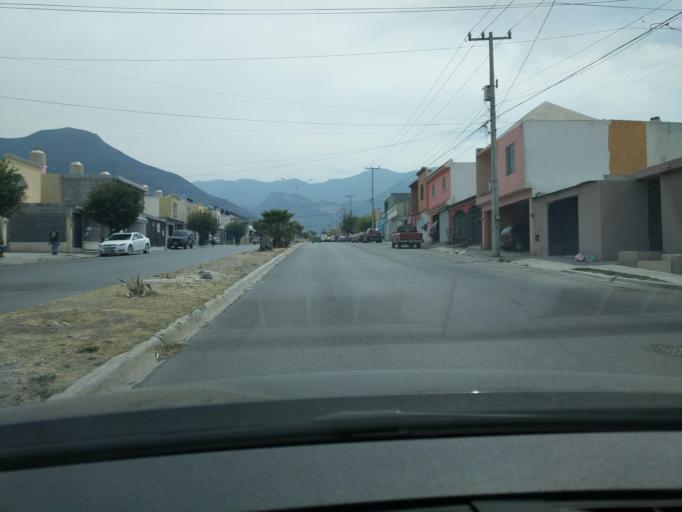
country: MX
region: Coahuila
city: Saltillo
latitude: 25.3530
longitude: -101.0143
